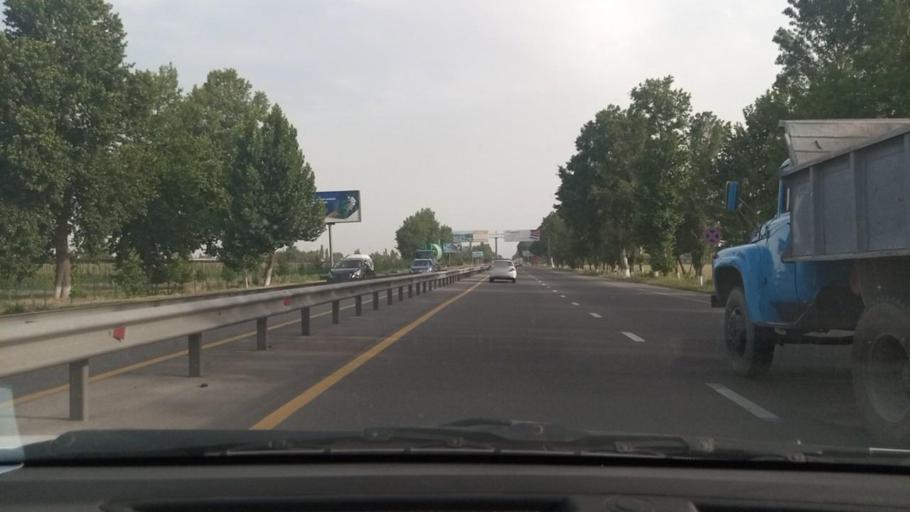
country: UZ
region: Toshkent Shahri
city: Bektemir
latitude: 41.2315
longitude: 69.4022
